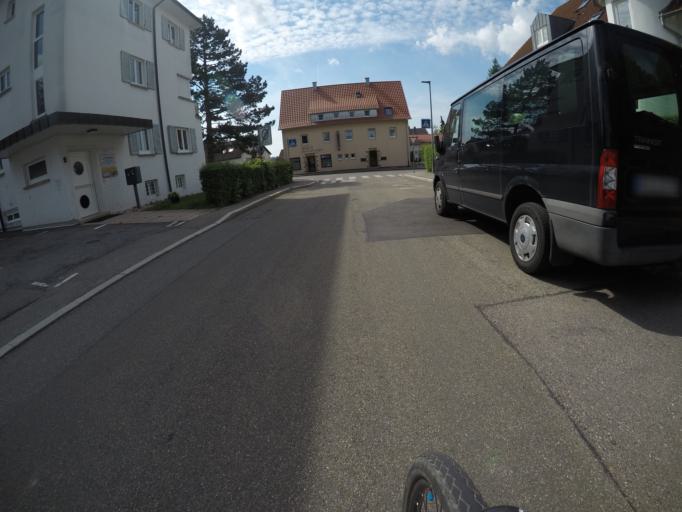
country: DE
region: Baden-Wuerttemberg
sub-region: Regierungsbezirk Stuttgart
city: Boeblingen
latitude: 48.6872
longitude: 9.0215
